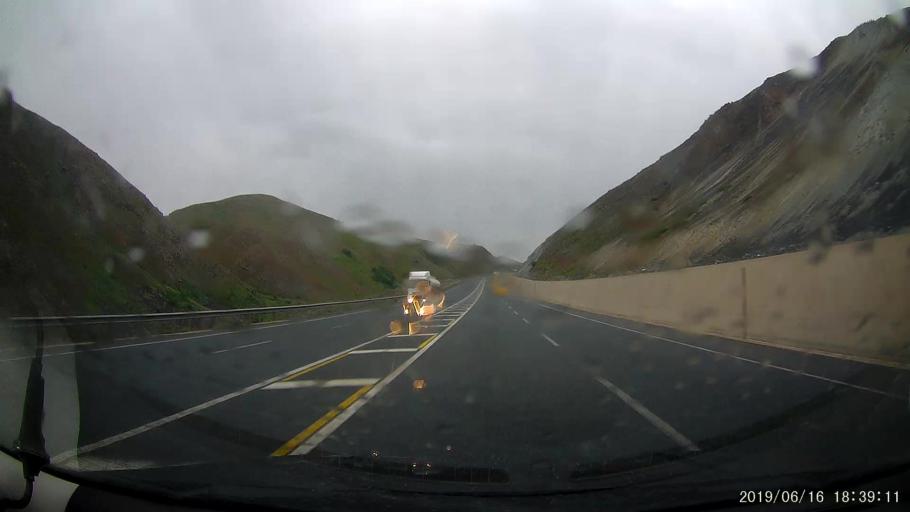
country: TR
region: Erzincan
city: Catalarmut
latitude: 39.8825
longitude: 39.1705
